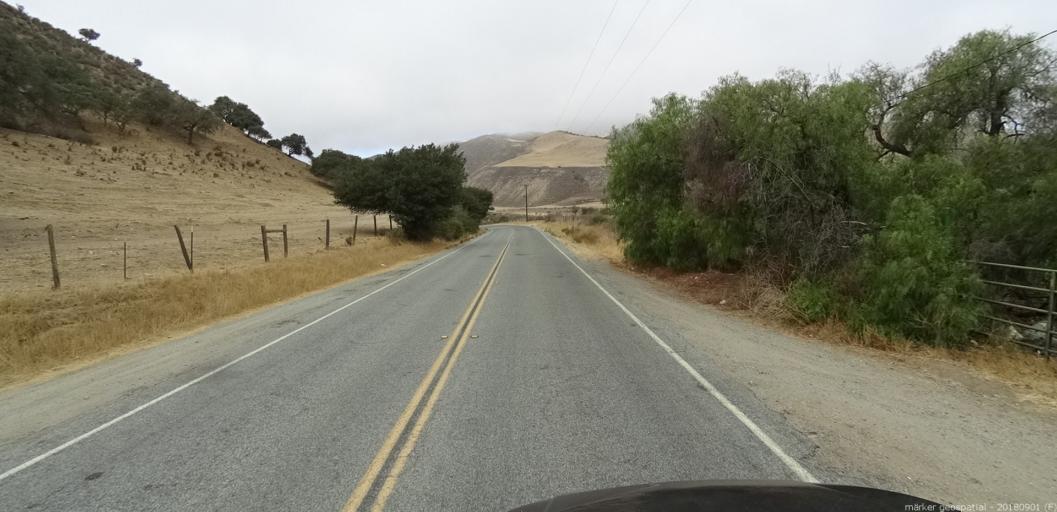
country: US
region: California
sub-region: Monterey County
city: Greenfield
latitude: 36.2794
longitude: -121.3151
